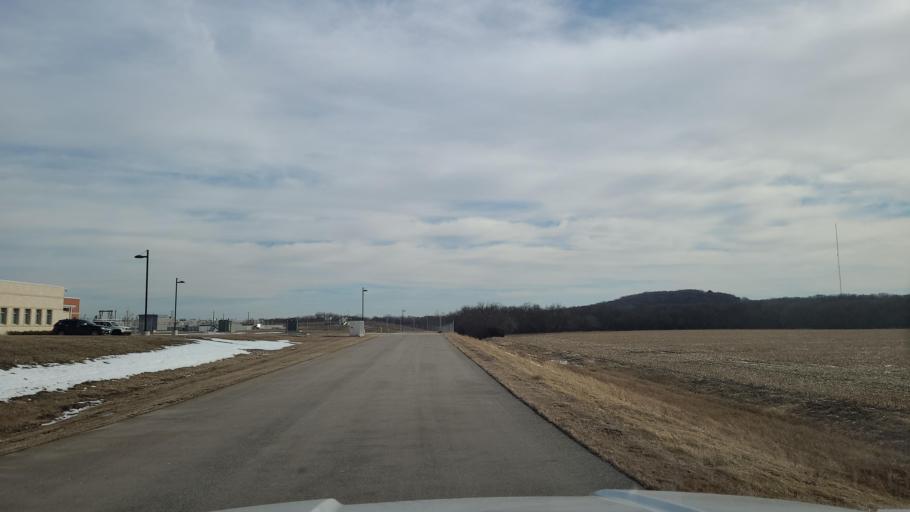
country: US
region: Kansas
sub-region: Douglas County
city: Lawrence
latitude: 38.9101
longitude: -95.2024
